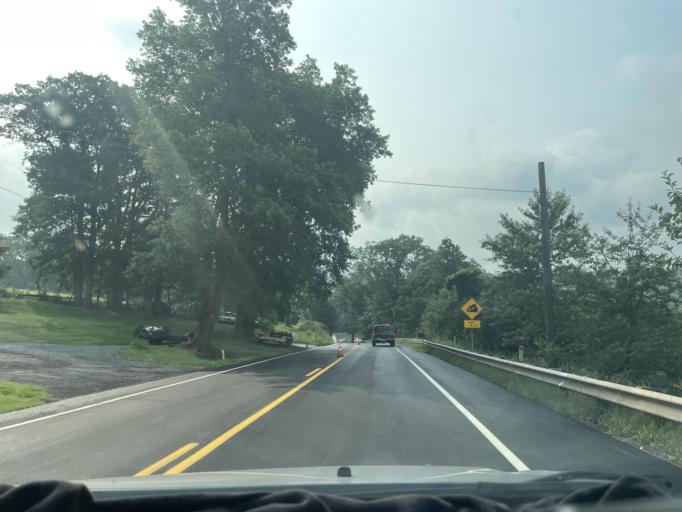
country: US
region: Maryland
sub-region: Garrett County
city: Mountain Lake Park
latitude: 39.2896
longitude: -79.3513
